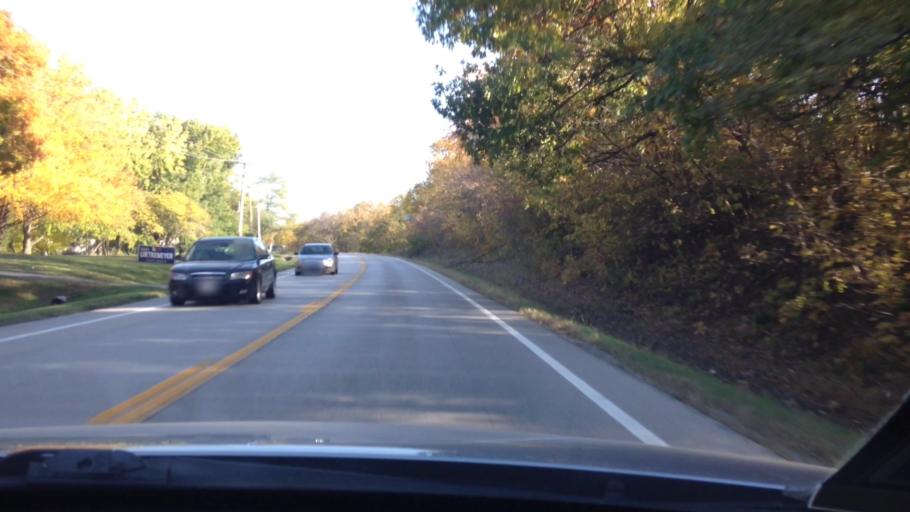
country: US
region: Missouri
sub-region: Platte County
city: Weatherby Lake
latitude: 39.2282
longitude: -94.7770
